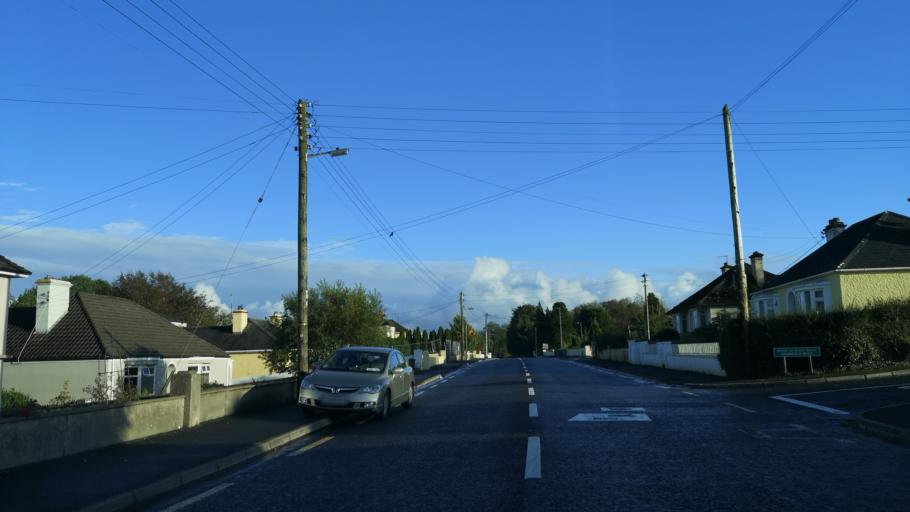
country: IE
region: Connaught
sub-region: Roscommon
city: Castlerea
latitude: 53.7640
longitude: -8.4781
